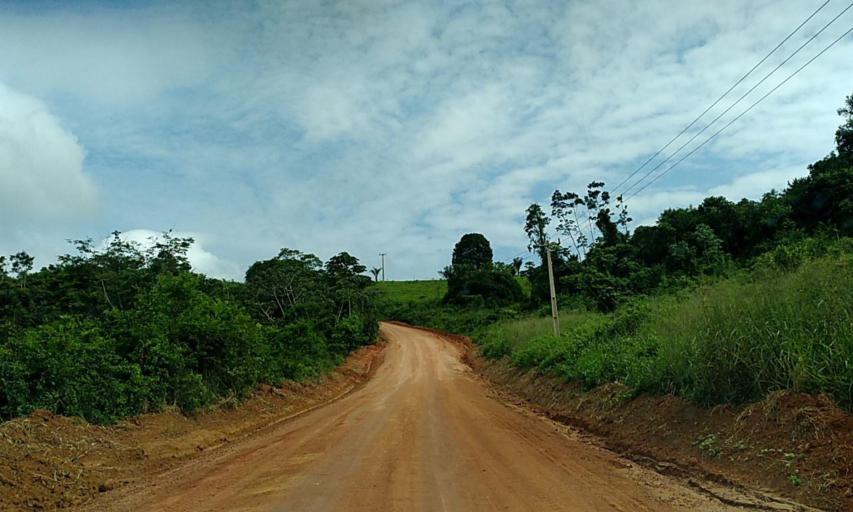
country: BR
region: Para
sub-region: Senador Jose Porfirio
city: Senador Jose Porfirio
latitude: -3.0687
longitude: -51.6349
